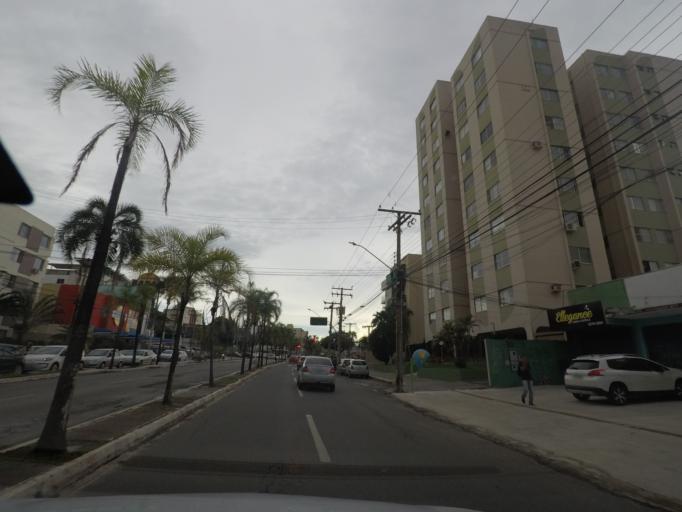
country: BR
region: Goias
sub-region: Goiania
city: Goiania
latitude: -16.6988
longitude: -49.2525
